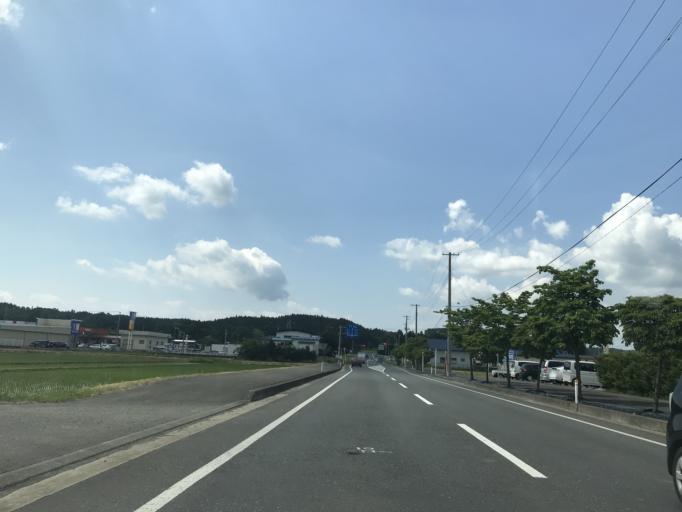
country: JP
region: Miyagi
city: Furukawa
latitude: 38.7358
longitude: 140.9591
